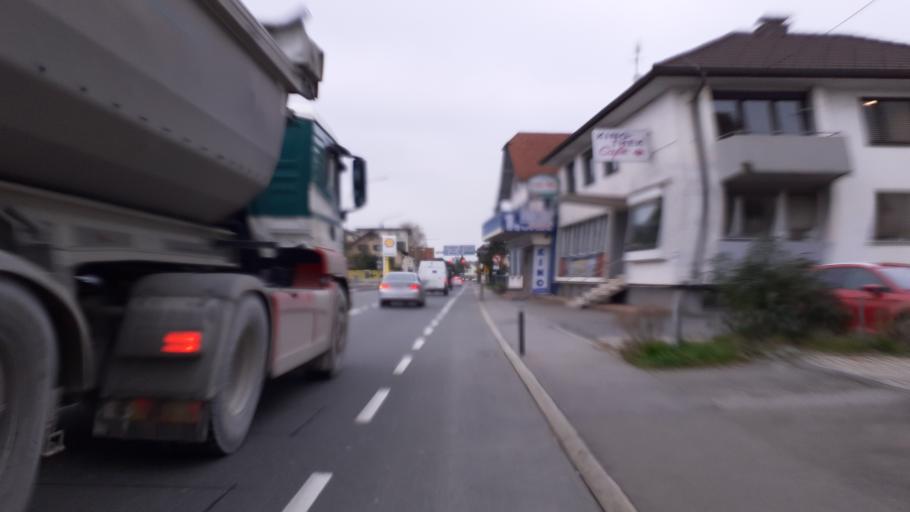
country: AT
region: Vorarlberg
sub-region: Politischer Bezirk Dornbirn
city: Lustenau
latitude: 47.4300
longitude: 9.6497
